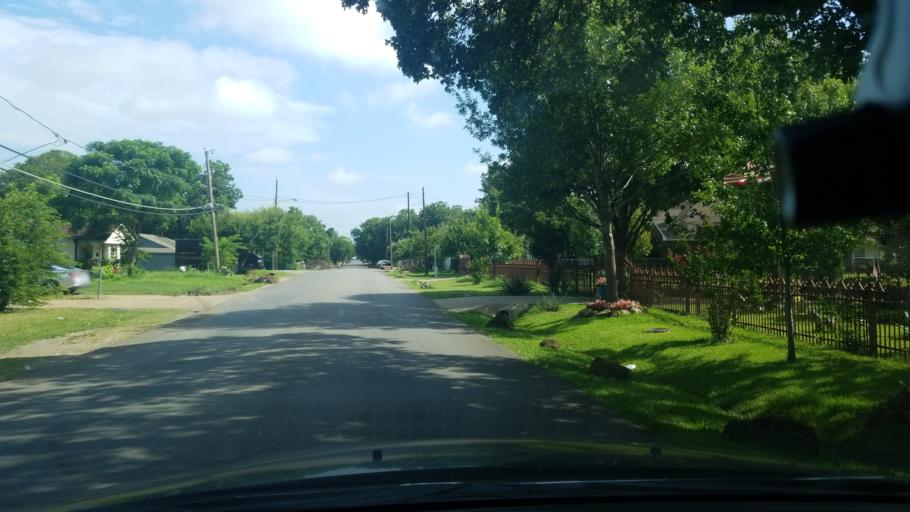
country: US
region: Texas
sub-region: Dallas County
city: Balch Springs
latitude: 32.7494
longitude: -96.6801
